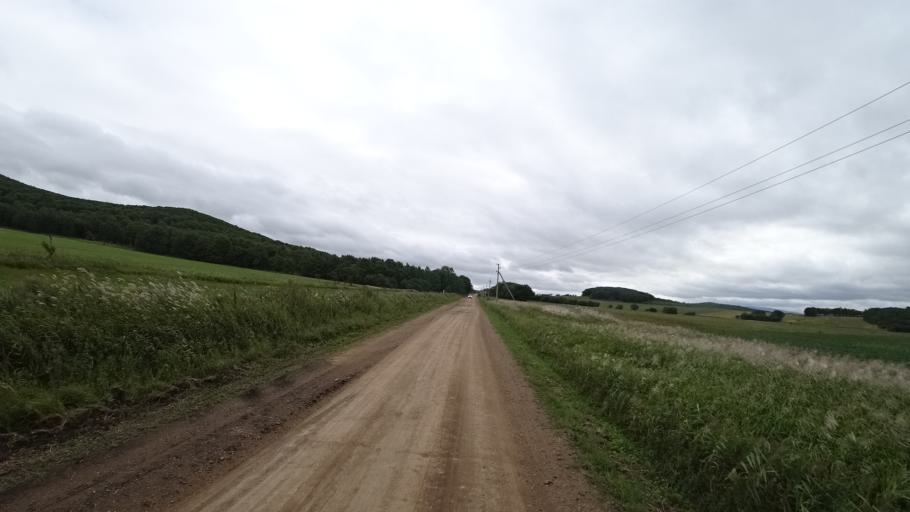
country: RU
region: Primorskiy
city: Chernigovka
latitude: 44.4704
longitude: 132.5823
